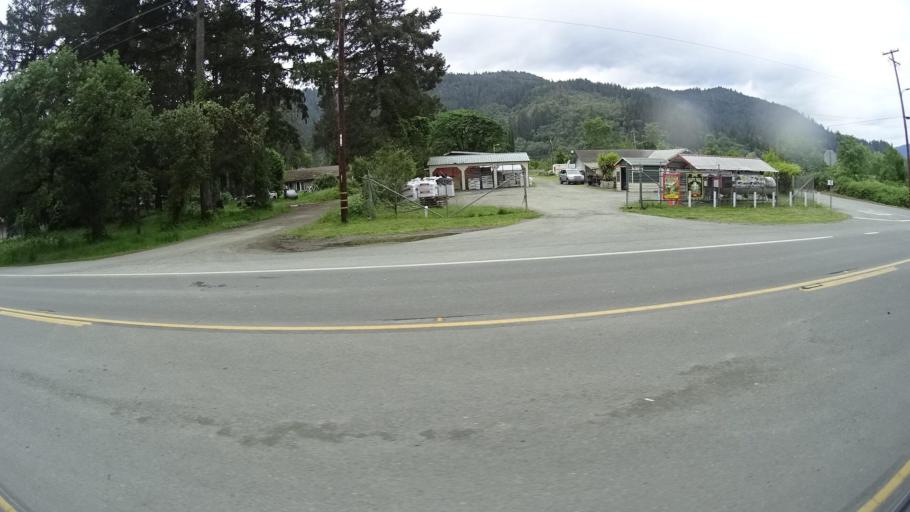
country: US
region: California
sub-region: Humboldt County
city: Willow Creek
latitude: 41.0667
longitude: -123.6863
